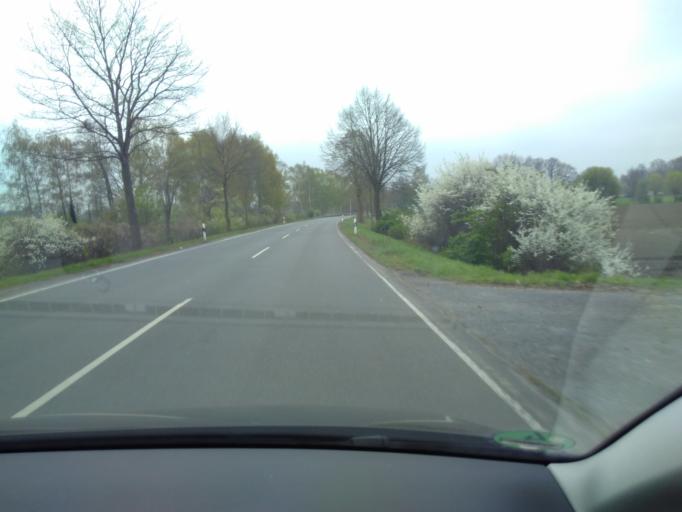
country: DE
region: North Rhine-Westphalia
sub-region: Regierungsbezirk Detmold
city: Verl
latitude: 51.8343
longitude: 8.5654
